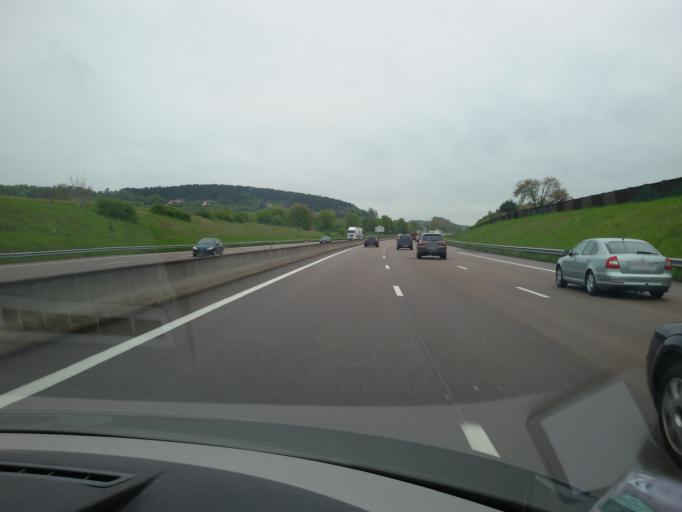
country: FR
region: Bourgogne
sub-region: Departement de Saone-et-Loire
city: Tournus
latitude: 46.5680
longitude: 4.8957
